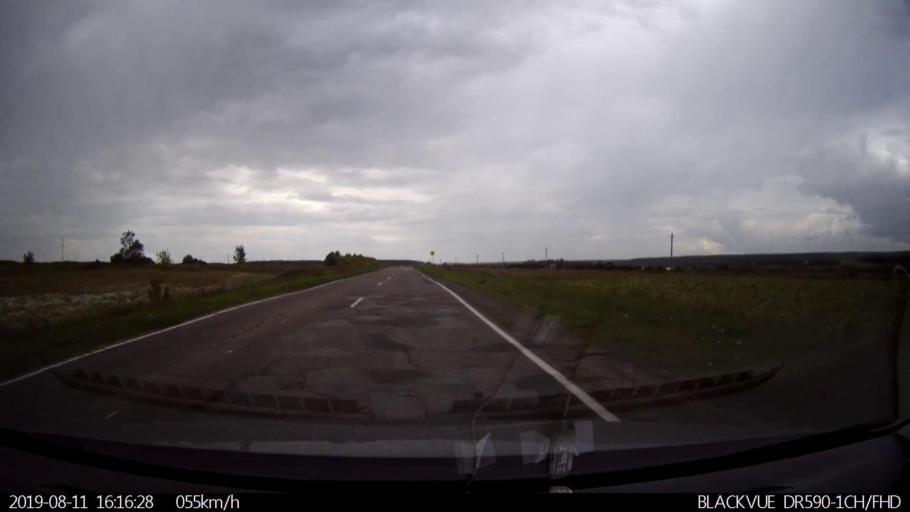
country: RU
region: Ulyanovsk
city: Mayna
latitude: 54.0413
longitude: 47.6212
